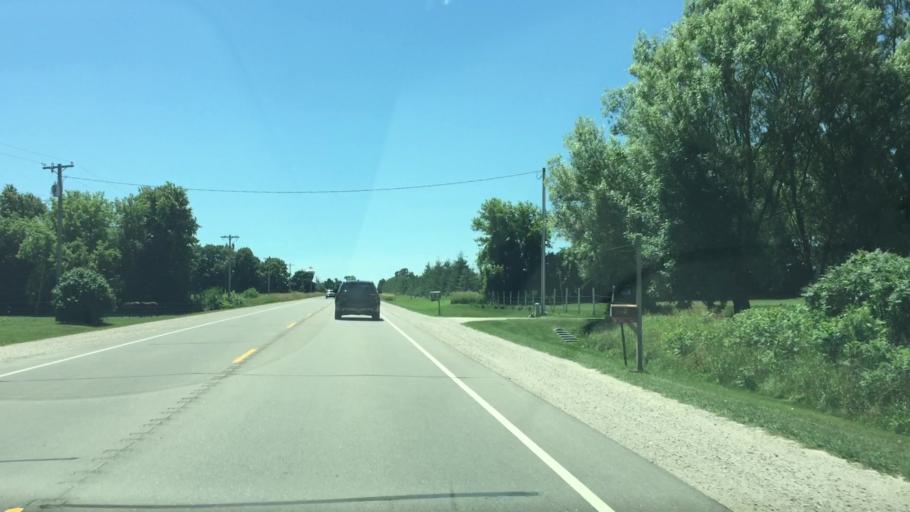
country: US
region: Wisconsin
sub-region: Calumet County
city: New Holstein
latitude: 43.9689
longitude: -88.1124
